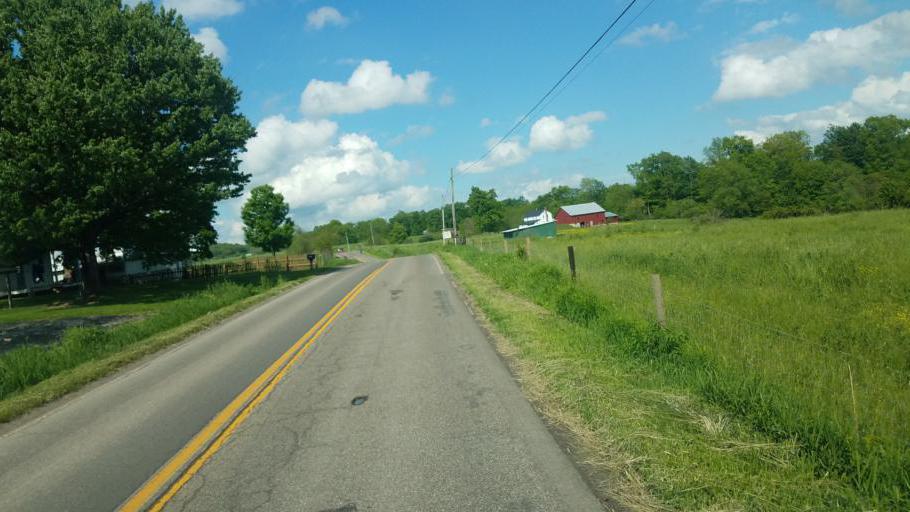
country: US
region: Ohio
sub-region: Wayne County
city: Apple Creek
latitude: 40.6984
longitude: -81.8477
